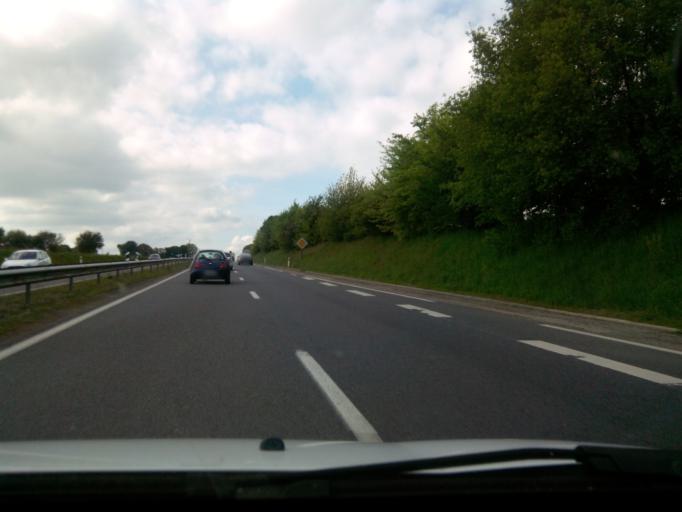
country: FR
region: Brittany
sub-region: Departement des Cotes-d'Armor
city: Pedernec
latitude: 48.6036
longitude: -3.2712
